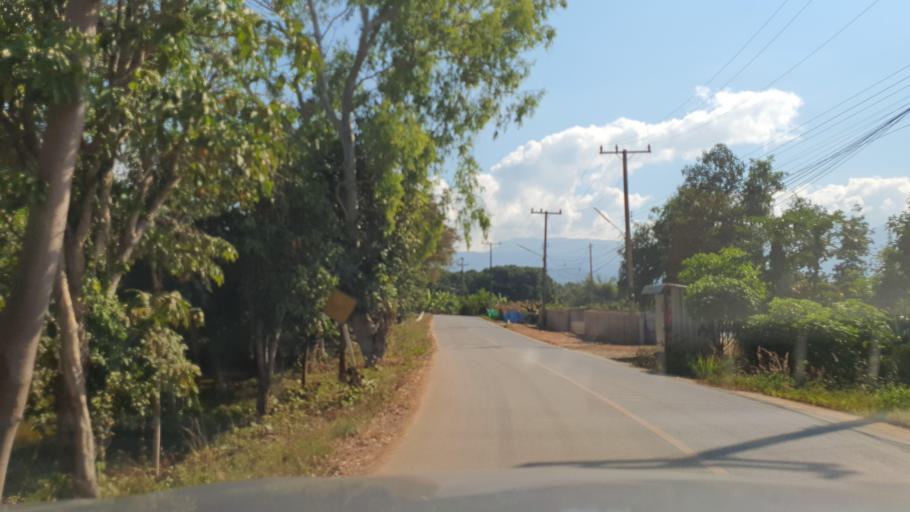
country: TH
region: Nan
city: Pua
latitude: 19.1410
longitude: 100.9251
